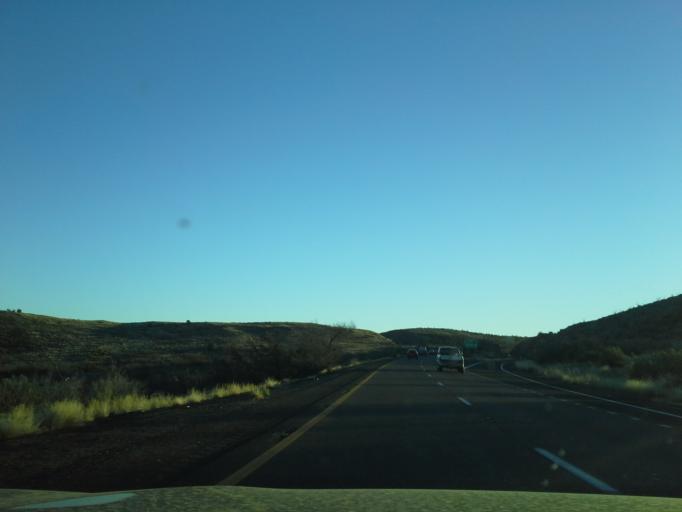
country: US
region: Arizona
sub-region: Yavapai County
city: Cordes Lakes
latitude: 34.2403
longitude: -112.1146
